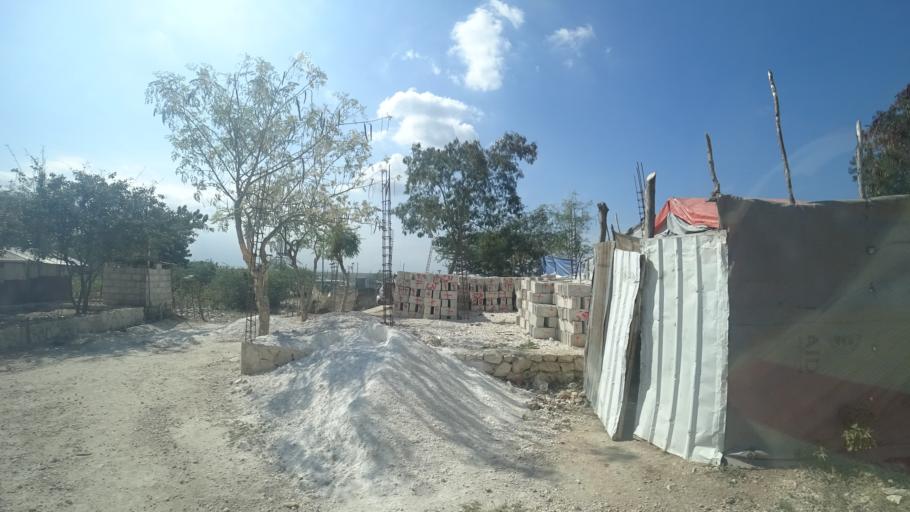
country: HT
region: Ouest
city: Croix des Bouquets
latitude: 18.6608
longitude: -72.2902
